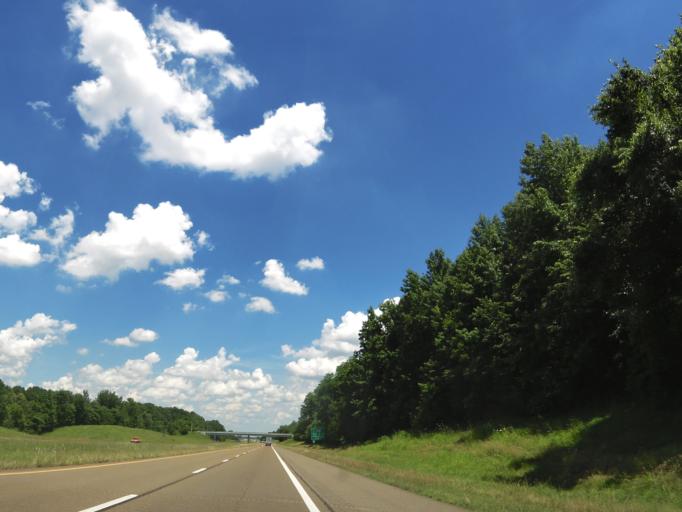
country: US
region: Tennessee
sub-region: Dyer County
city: Dyersburg
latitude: 36.0692
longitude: -89.4225
